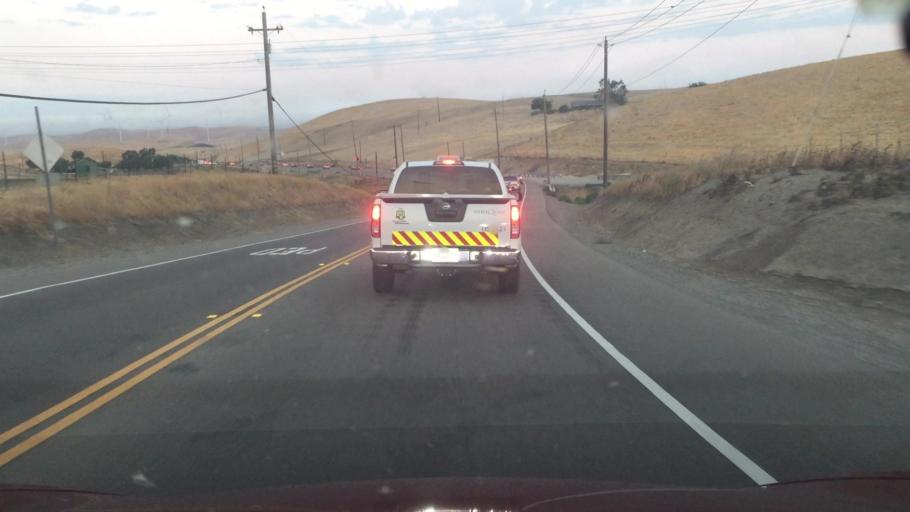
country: US
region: California
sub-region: San Joaquin County
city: Mountain House
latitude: 37.7496
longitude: -121.5775
